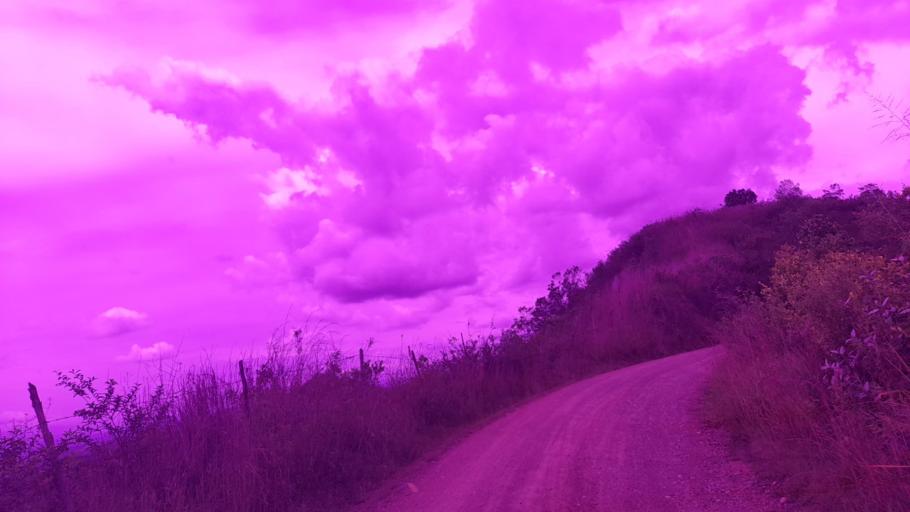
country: CO
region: Valle del Cauca
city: Andalucia
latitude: 4.1755
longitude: -76.1146
